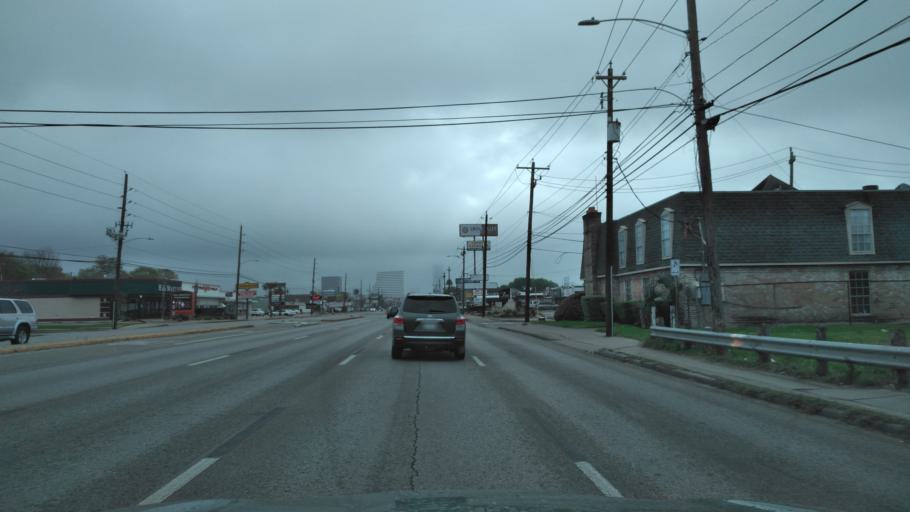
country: US
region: Texas
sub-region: Harris County
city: Piney Point Village
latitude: 29.7376
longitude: -95.4957
